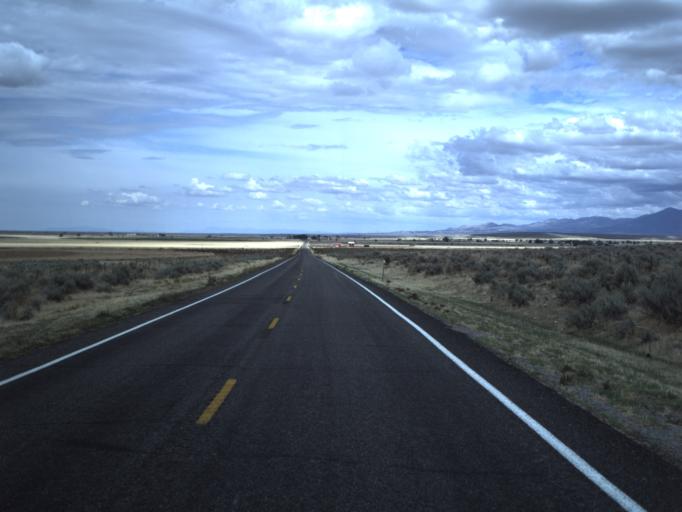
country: US
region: Utah
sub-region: Millard County
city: Fillmore
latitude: 39.0095
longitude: -112.4100
